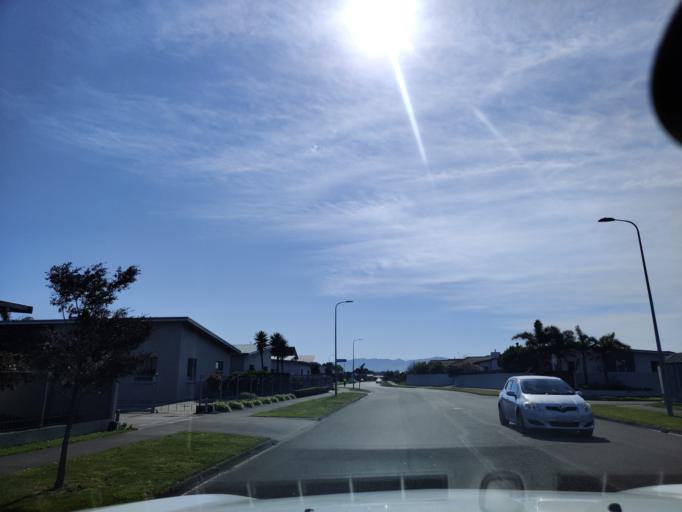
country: NZ
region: Manawatu-Wanganui
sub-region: Palmerston North City
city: Palmerston North
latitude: -40.3333
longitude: 175.6568
